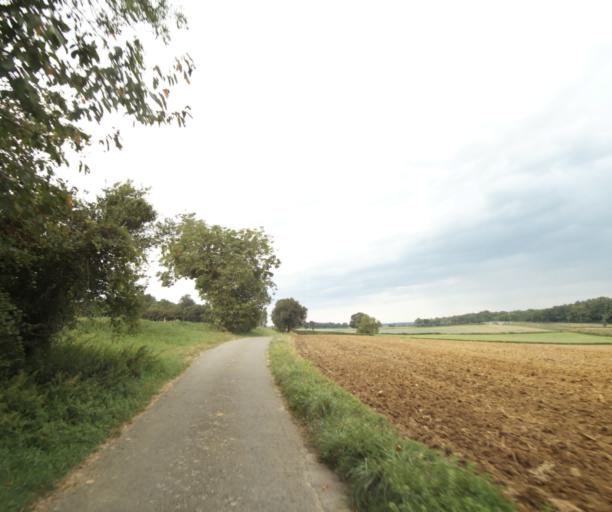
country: FR
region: Bourgogne
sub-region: Departement de Saone-et-Loire
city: Tournus
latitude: 46.5930
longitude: 4.9079
